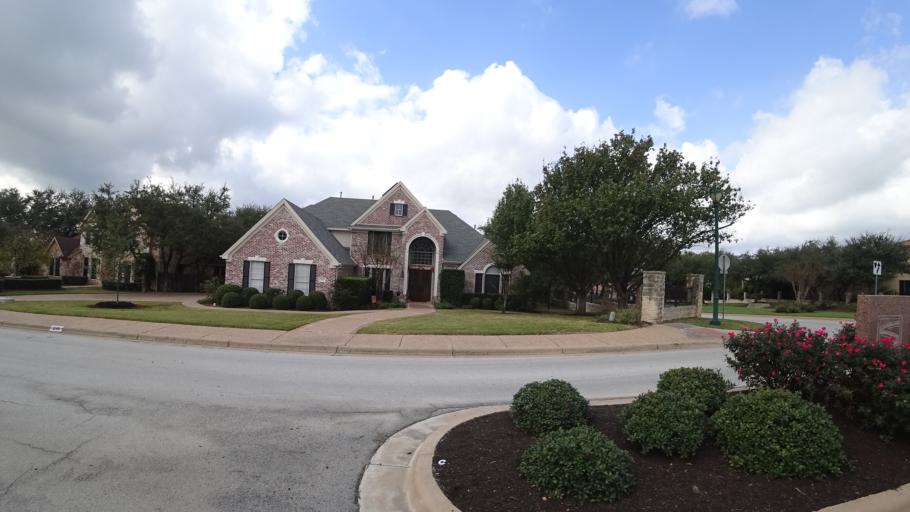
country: US
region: Texas
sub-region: Travis County
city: Bee Cave
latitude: 30.3112
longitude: -97.9028
